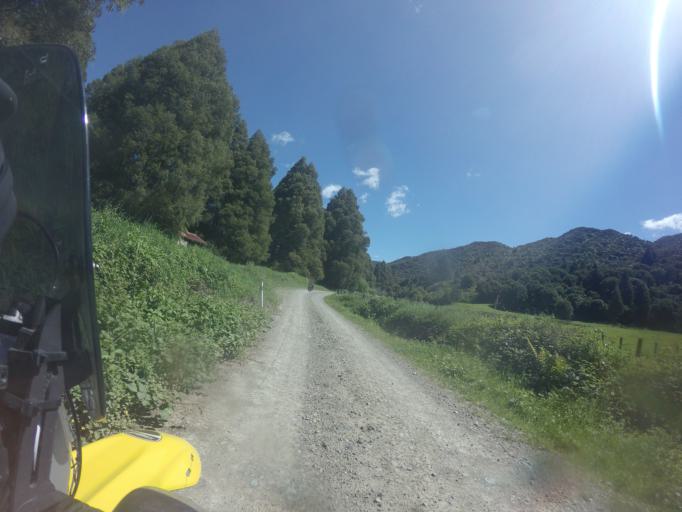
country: NZ
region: Bay of Plenty
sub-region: Opotiki District
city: Opotiki
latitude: -38.2958
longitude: 177.3373
